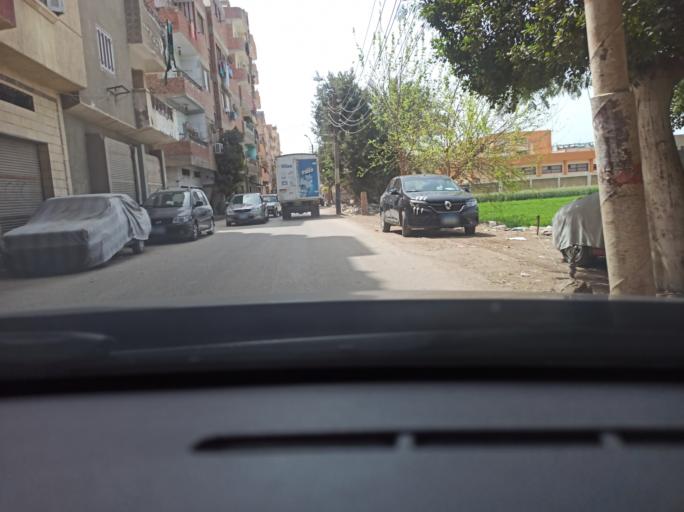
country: EG
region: Muhafazat Bani Suwayf
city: Bani Suwayf
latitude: 29.0793
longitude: 31.0877
